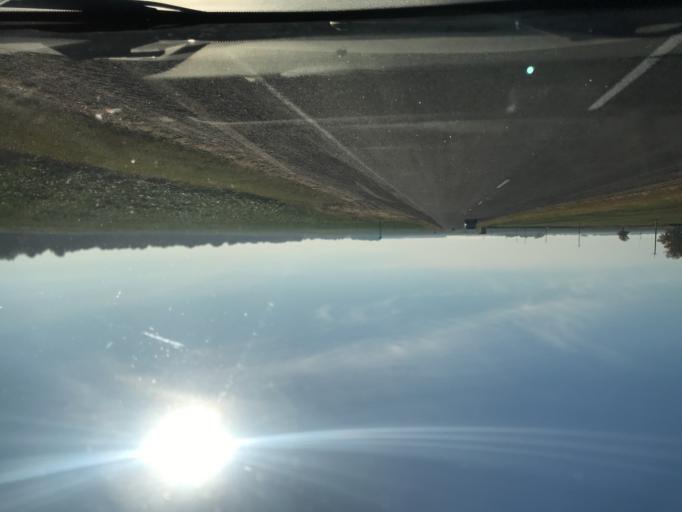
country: BY
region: Gomel
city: Brahin
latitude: 51.7982
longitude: 30.1389
